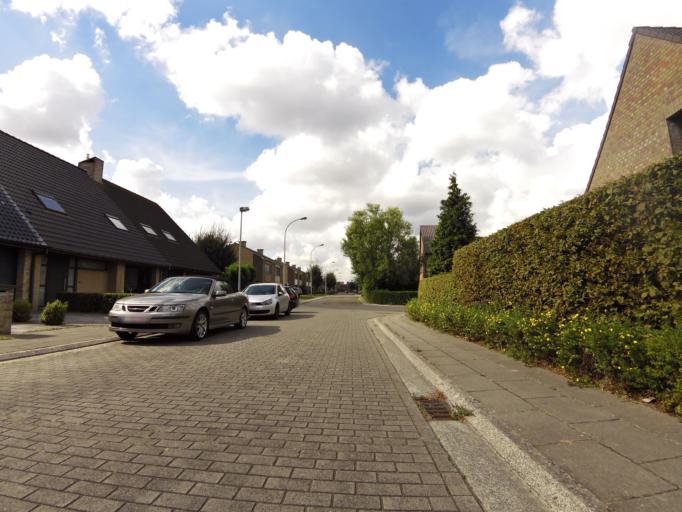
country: BE
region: Flanders
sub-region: Provincie West-Vlaanderen
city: Sint-Kruis
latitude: 51.2302
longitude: 3.2454
